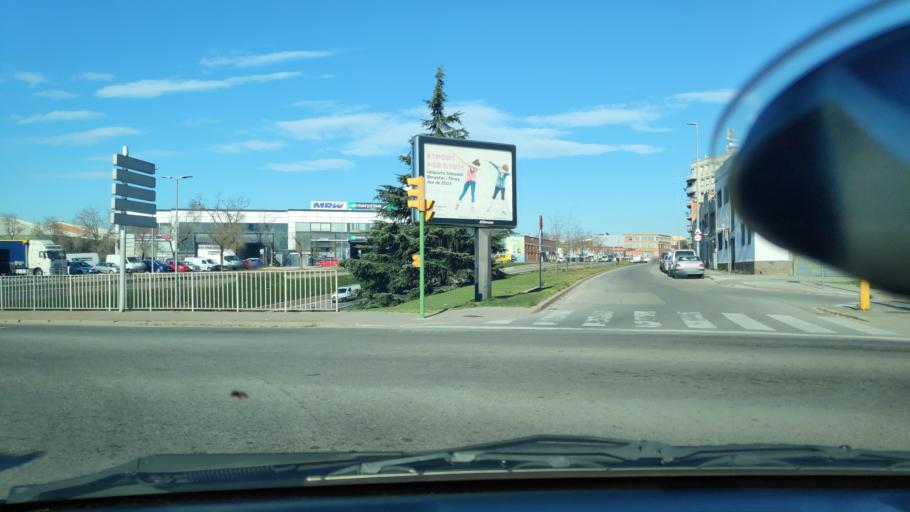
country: ES
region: Catalonia
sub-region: Provincia de Barcelona
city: Sabadell
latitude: 41.5325
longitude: 2.1042
